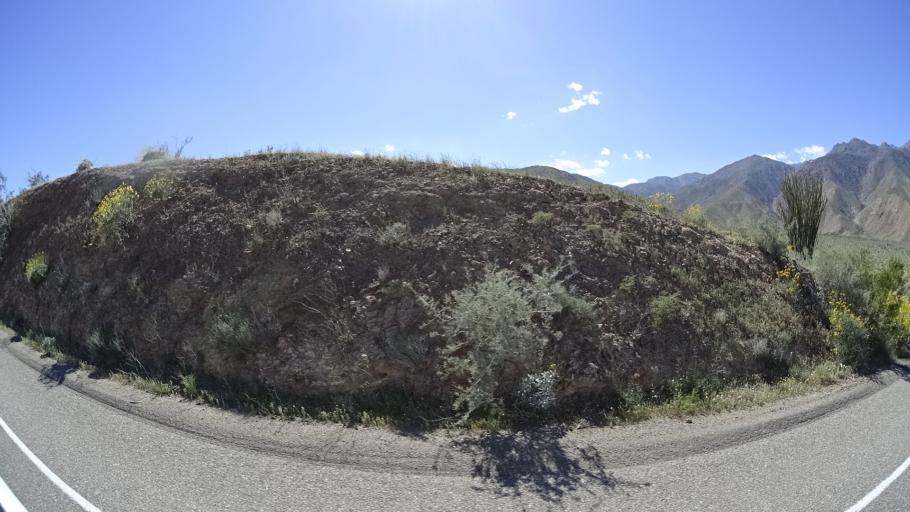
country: US
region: California
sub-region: San Diego County
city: Borrego Springs
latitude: 33.2455
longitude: -116.4025
